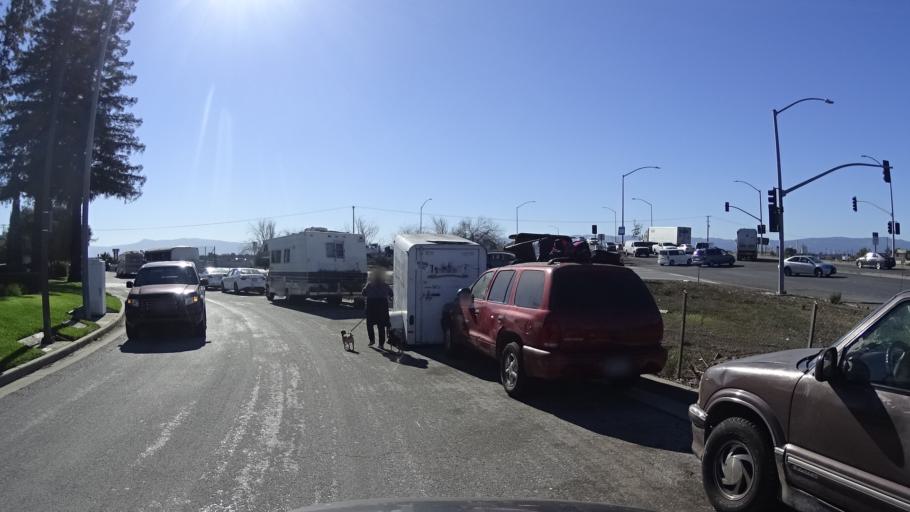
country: US
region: California
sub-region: Santa Clara County
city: Santa Clara
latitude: 37.3775
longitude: -121.9402
